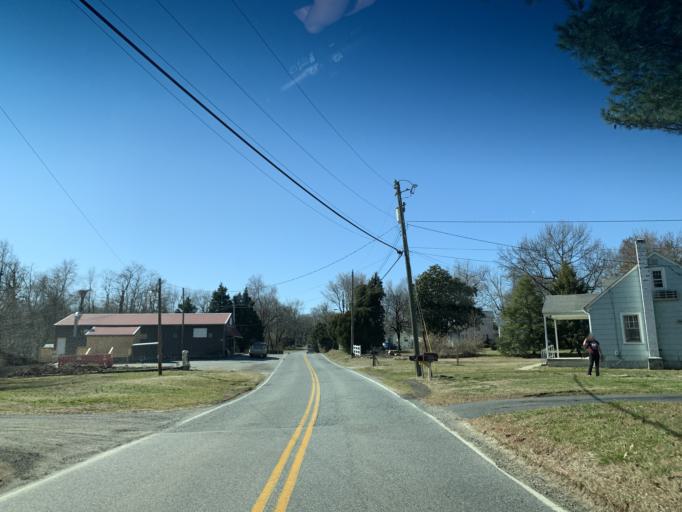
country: US
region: Maryland
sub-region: Cecil County
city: Charlestown
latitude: 39.4632
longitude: -75.8797
